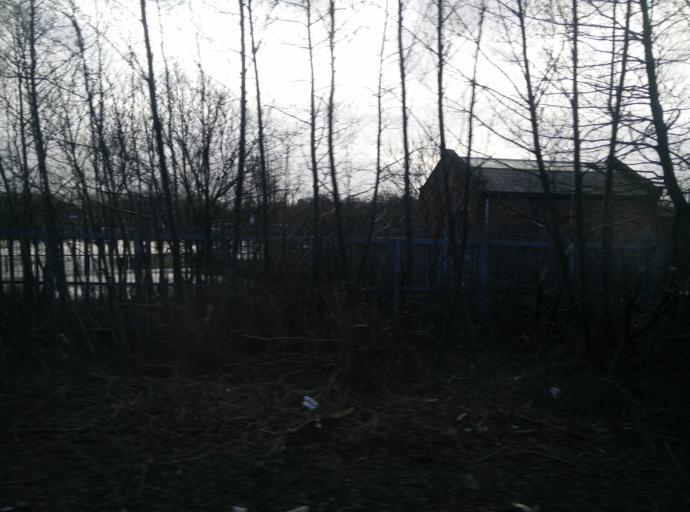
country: GB
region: Northern Ireland
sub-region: City of Belfast
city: Belfast
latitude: 54.5904
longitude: -5.9215
